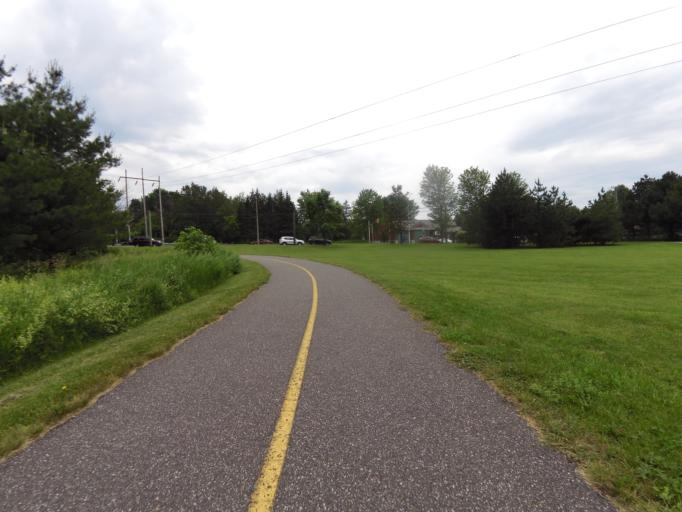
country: CA
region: Ontario
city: Bells Corners
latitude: 45.3529
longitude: -75.7627
